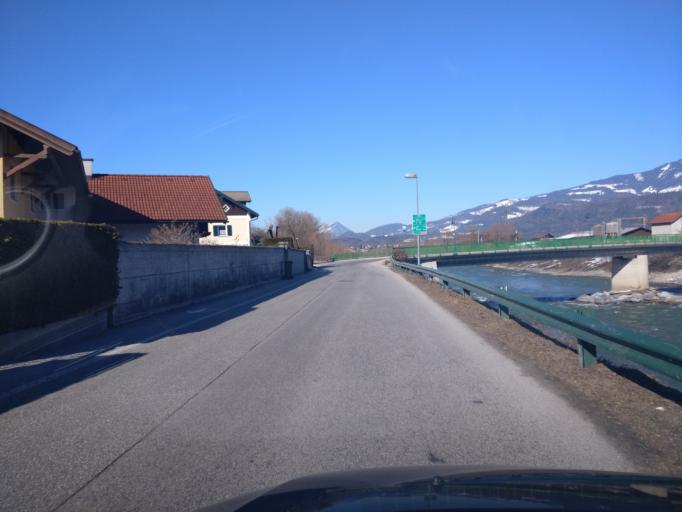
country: AT
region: Salzburg
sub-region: Politischer Bezirk Hallein
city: Kuchl
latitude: 47.6245
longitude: 13.1379
